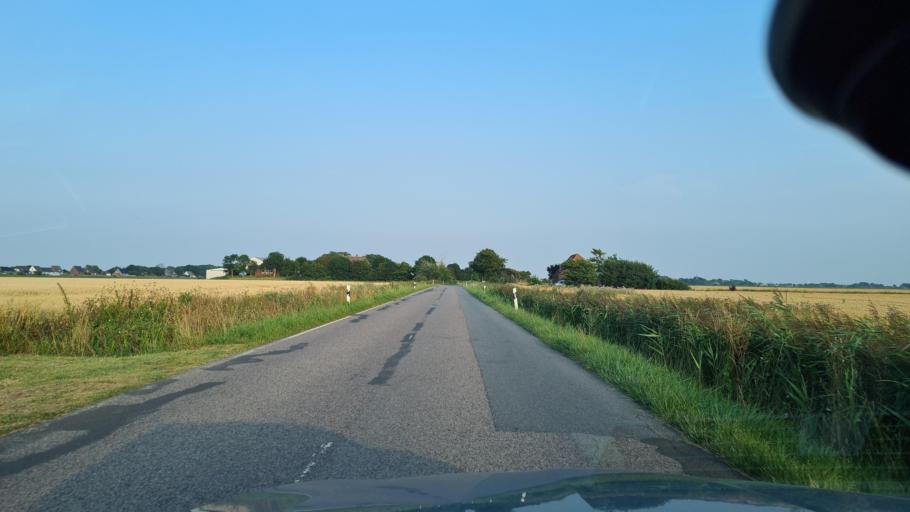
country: DE
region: Schleswig-Holstein
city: Elisabeth-Sophien-Koog
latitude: 54.5048
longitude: 8.8305
